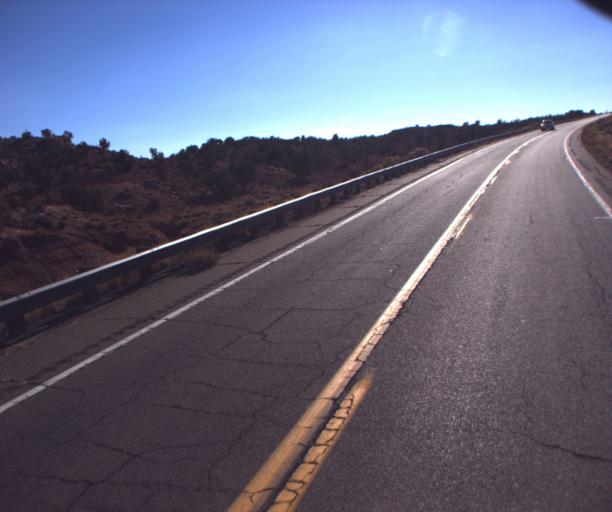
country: US
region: Arizona
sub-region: Coconino County
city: Kaibito
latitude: 36.6085
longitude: -111.0785
